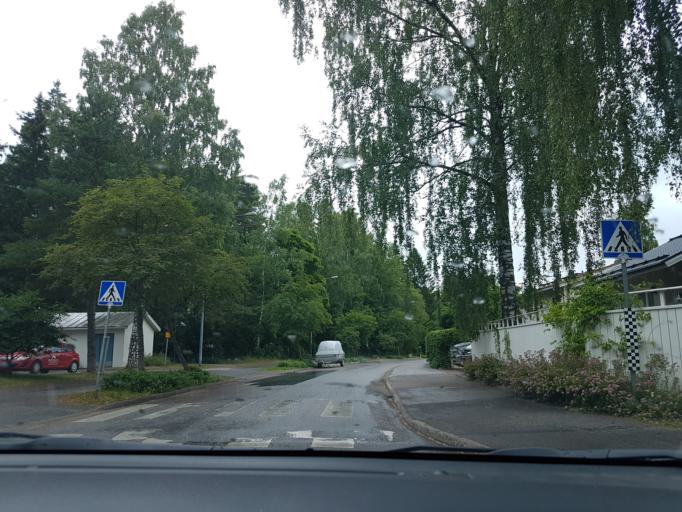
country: FI
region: Uusimaa
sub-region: Helsinki
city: Vantaa
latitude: 60.2416
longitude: 25.0926
